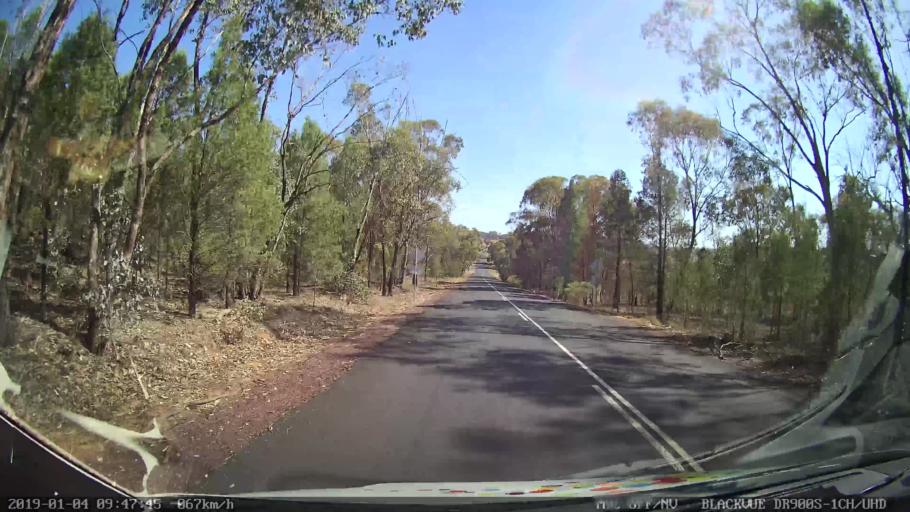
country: AU
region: New South Wales
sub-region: Cabonne
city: Canowindra
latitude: -33.6033
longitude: 148.4316
